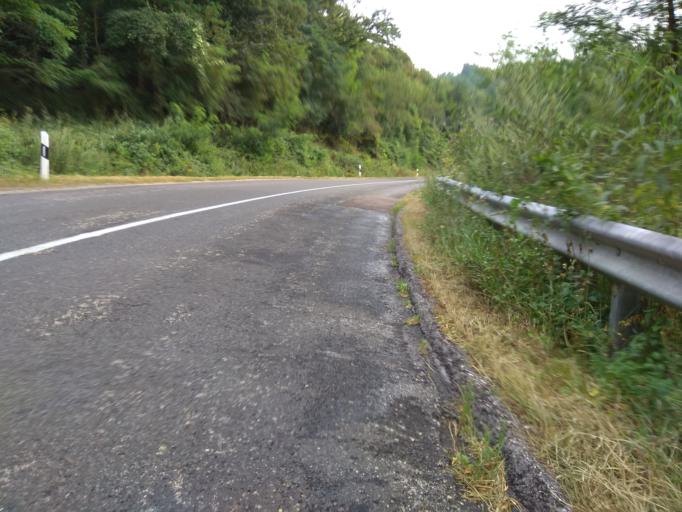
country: HU
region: Heves
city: Tarnalelesz
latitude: 48.0569
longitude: 20.2136
